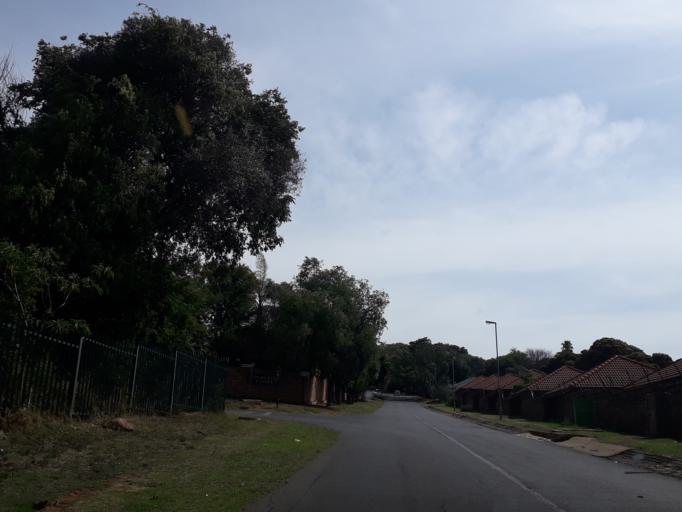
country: ZA
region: Gauteng
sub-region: City of Johannesburg Metropolitan Municipality
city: Roodepoort
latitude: -26.0728
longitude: 27.9576
